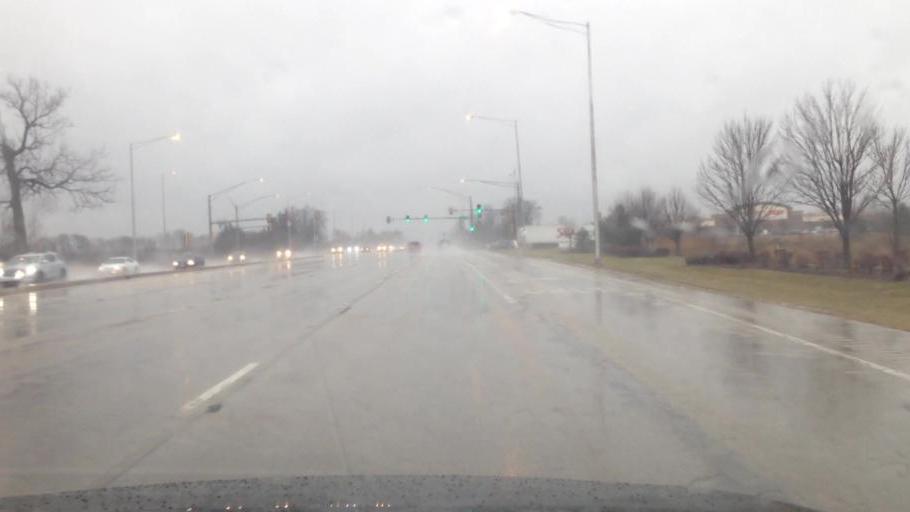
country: US
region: Illinois
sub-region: McHenry County
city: Lake in the Hills
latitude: 42.1482
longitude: -88.3359
